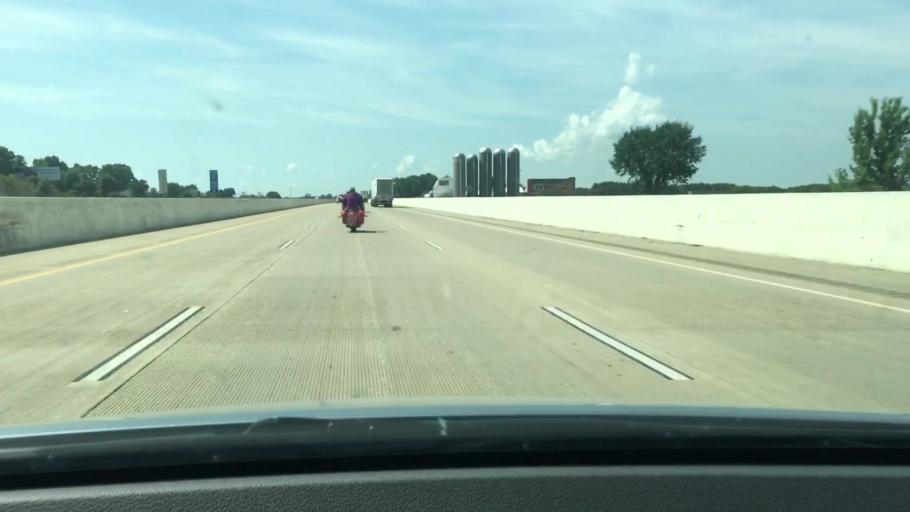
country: US
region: Wisconsin
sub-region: Winnebago County
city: Neenah
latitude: 44.1395
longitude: -88.4923
